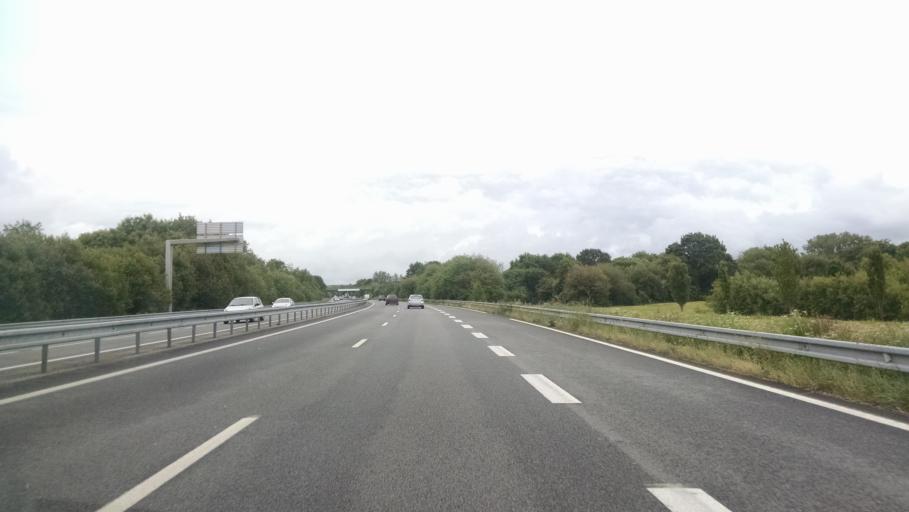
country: FR
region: Brittany
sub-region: Departement du Morbihan
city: Landevant
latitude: 47.7573
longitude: -3.1294
